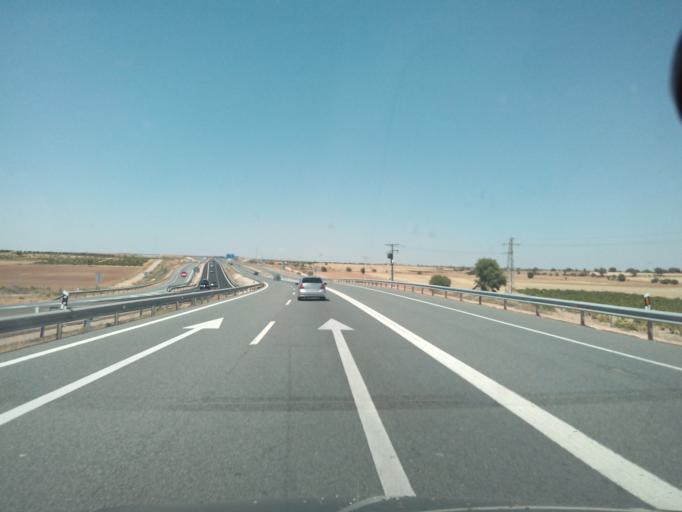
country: ES
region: Castille-La Mancha
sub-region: Province of Toledo
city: Dosbarrios
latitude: 39.8984
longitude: -3.4727
